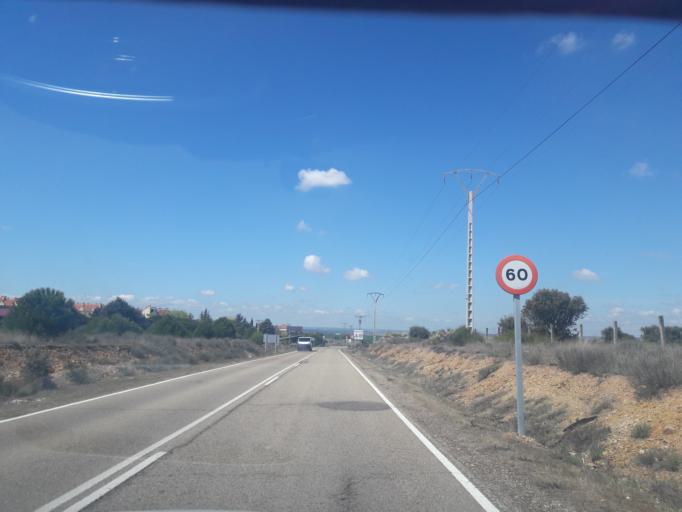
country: ES
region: Castille and Leon
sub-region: Provincia de Salamanca
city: Doninos de Salamanca
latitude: 40.9431
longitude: -5.7279
